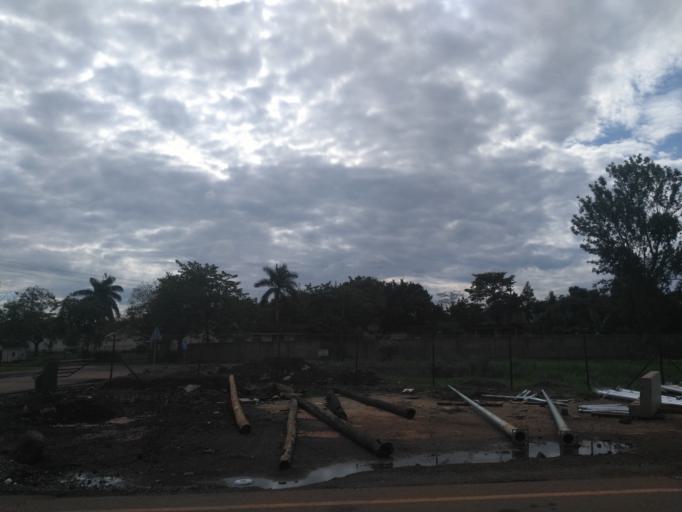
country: UG
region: Eastern Region
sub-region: Jinja District
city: Jinja
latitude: 0.4412
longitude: 33.1933
